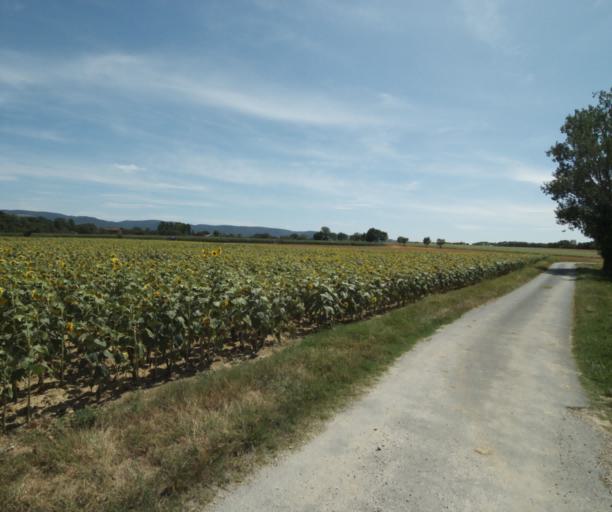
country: FR
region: Midi-Pyrenees
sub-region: Departement de la Haute-Garonne
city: Revel
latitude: 43.5087
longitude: 2.0197
